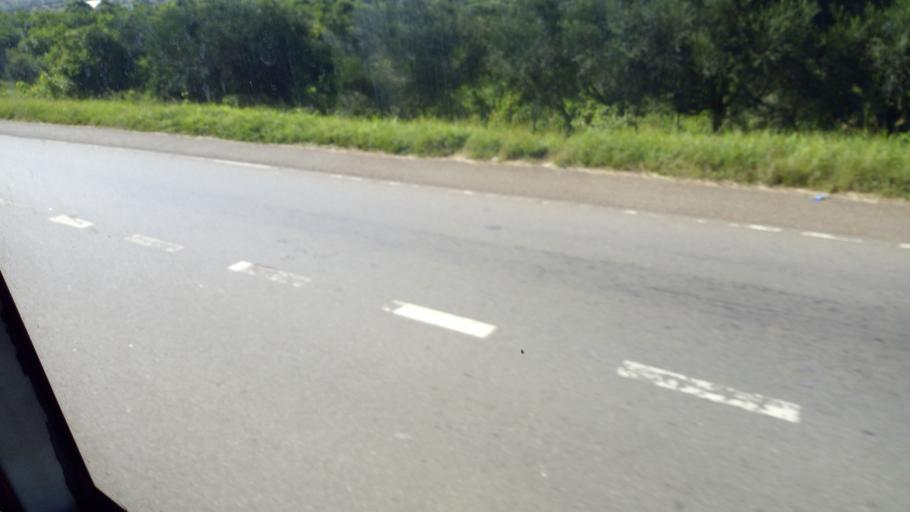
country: UG
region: Central Region
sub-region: Lyantonde District
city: Lyantonde
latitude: -0.4425
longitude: 31.0744
